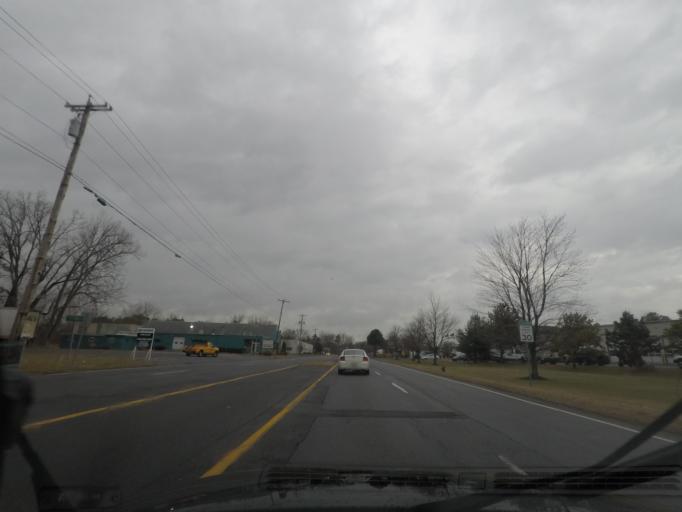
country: US
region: New York
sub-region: Albany County
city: Colonie
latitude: 42.7001
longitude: -73.8294
